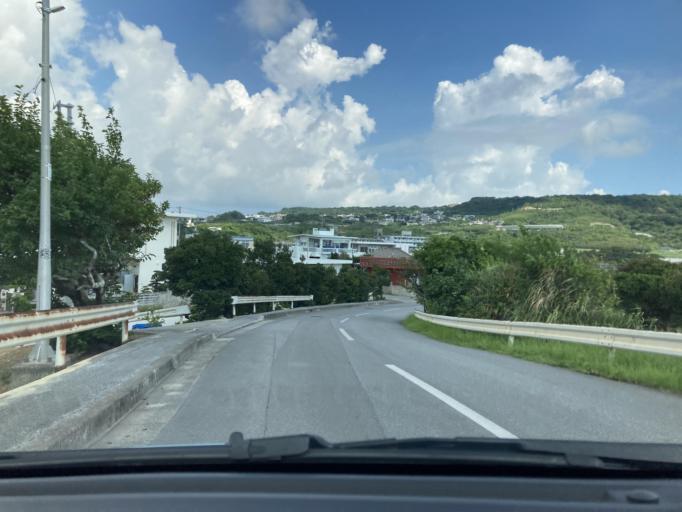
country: JP
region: Okinawa
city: Itoman
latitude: 26.1304
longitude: 127.7742
